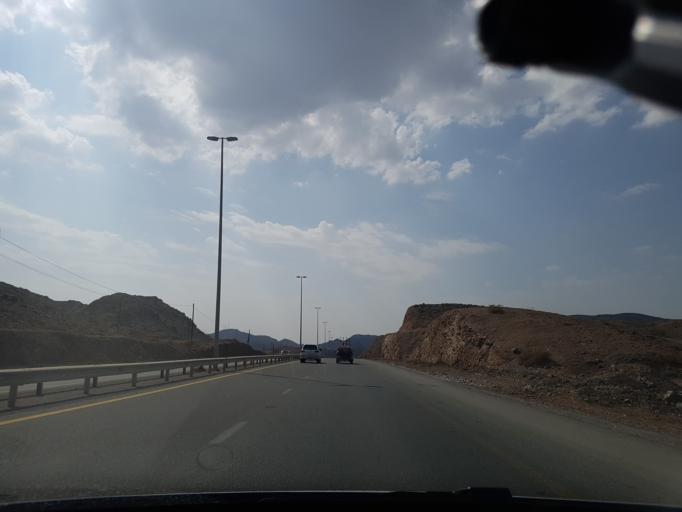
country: AE
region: Al Fujayrah
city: Dibba Al-Fujairah
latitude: 25.5161
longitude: 56.0849
